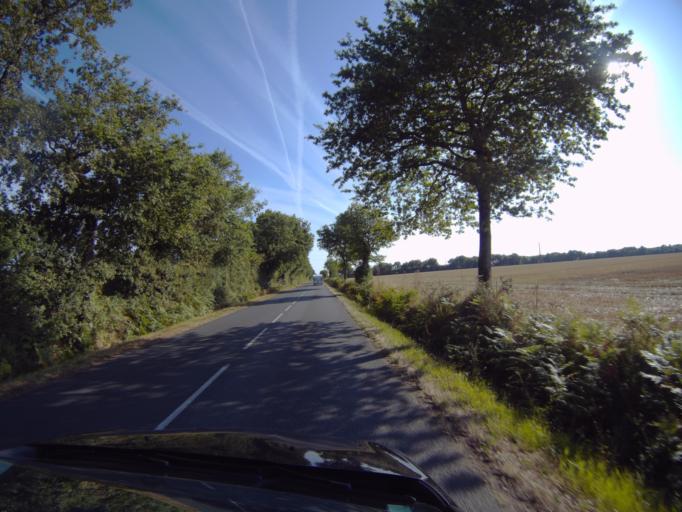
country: FR
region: Pays de la Loire
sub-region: Departement de la Vendee
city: Grosbreuil
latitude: 46.5160
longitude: -1.5604
